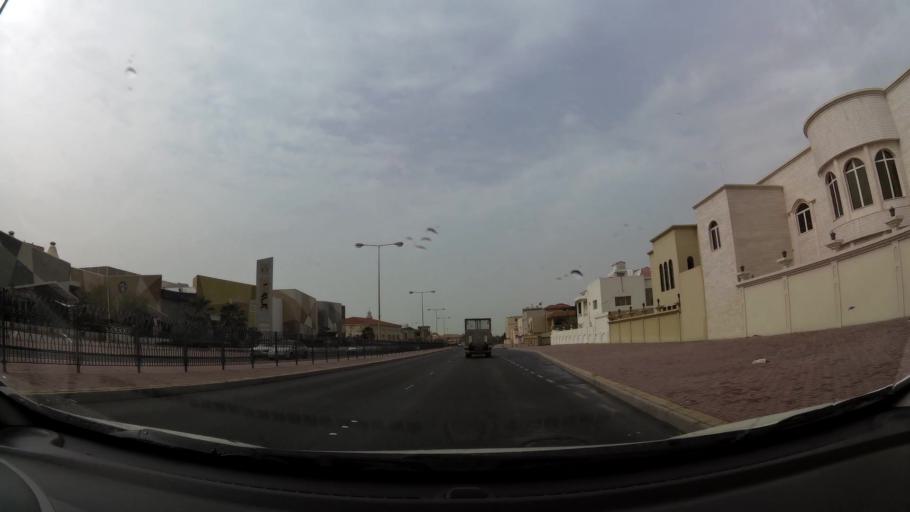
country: BH
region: Northern
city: Ar Rifa'
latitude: 26.1370
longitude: 50.5597
